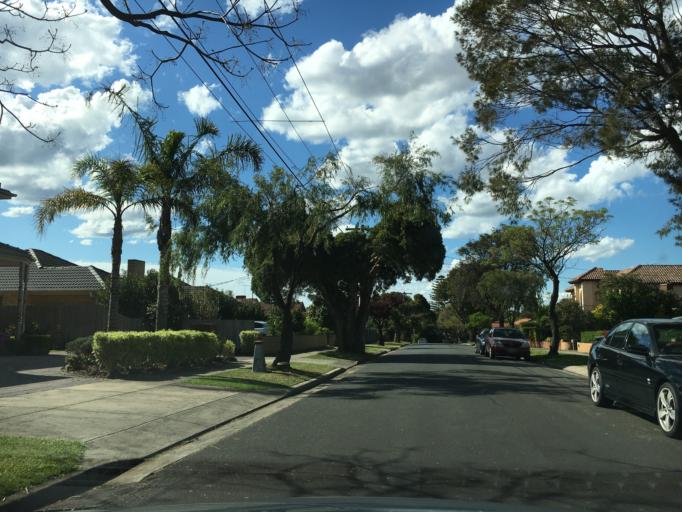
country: AU
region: Victoria
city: Clayton
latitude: -37.9014
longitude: 145.1177
